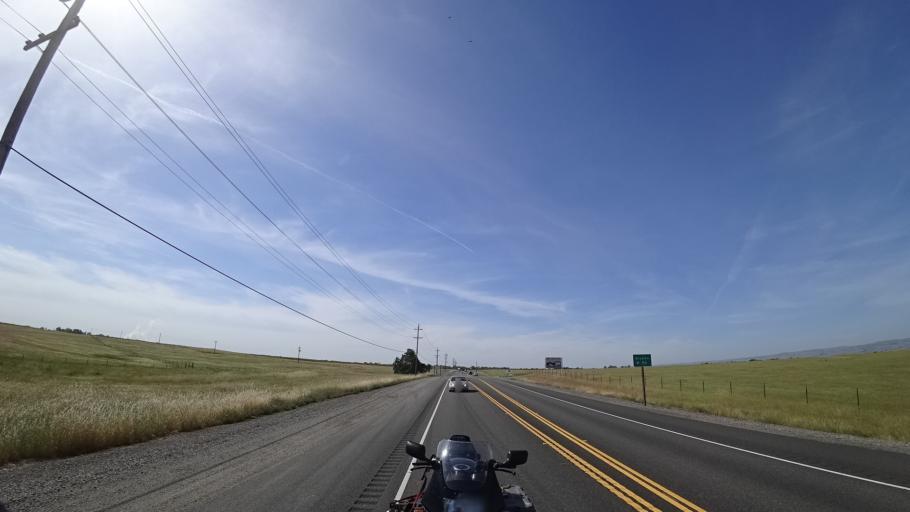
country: US
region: California
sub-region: Glenn County
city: Hamilton City
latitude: 39.8621
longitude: -121.9588
